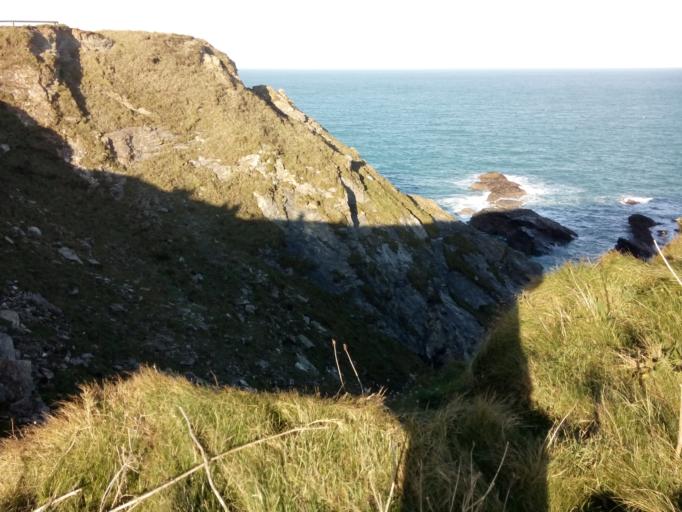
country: GB
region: England
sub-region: Cornwall
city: Hayle
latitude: 50.2394
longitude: -5.3908
